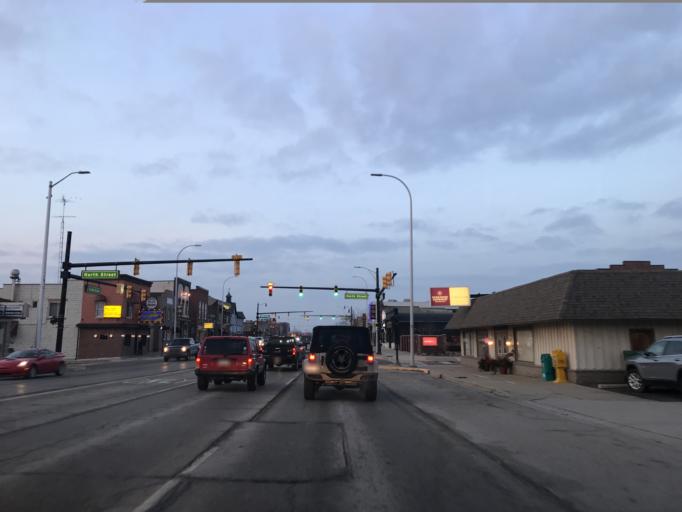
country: US
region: Michigan
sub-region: Livingston County
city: Brighton
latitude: 42.5283
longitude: -83.7796
